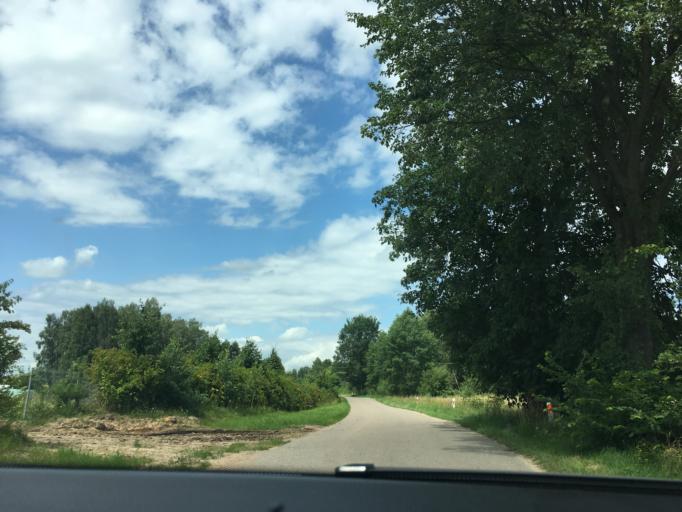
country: PL
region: Podlasie
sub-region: Powiat sejnenski
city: Krasnopol
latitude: 54.0937
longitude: 23.2370
